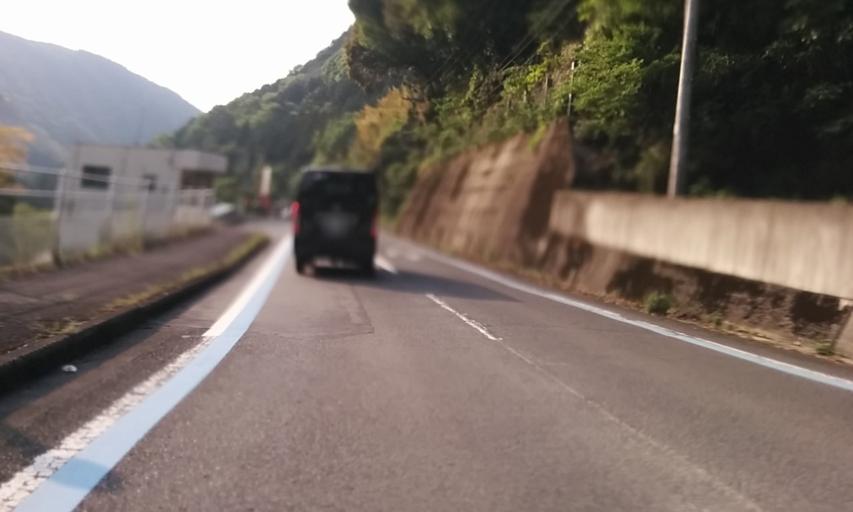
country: JP
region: Ehime
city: Saijo
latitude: 33.8657
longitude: 133.1850
